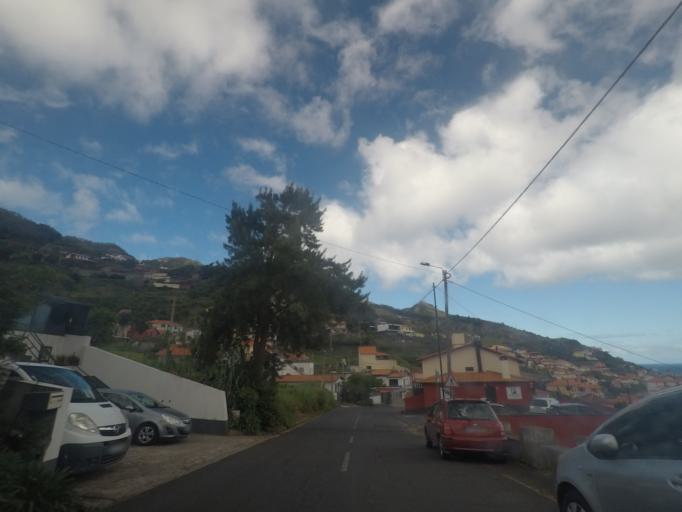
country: PT
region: Madeira
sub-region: Machico
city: Machico
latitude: 32.7304
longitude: -16.7727
